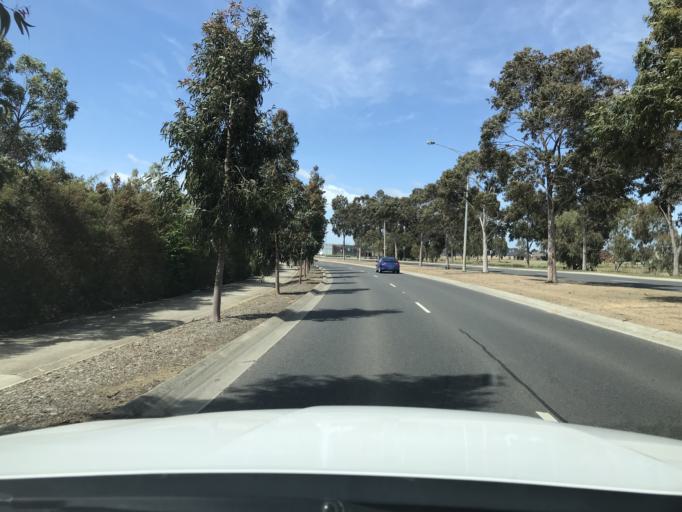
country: AU
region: Victoria
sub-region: Hume
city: Roxburgh Park
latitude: -37.6173
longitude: 144.9267
